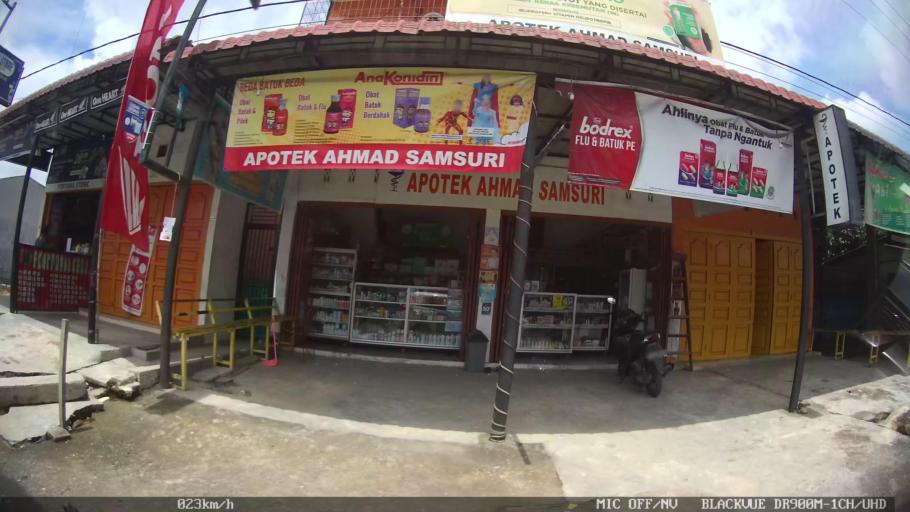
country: ID
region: North Sumatra
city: Medan
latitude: 3.6138
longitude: 98.7480
